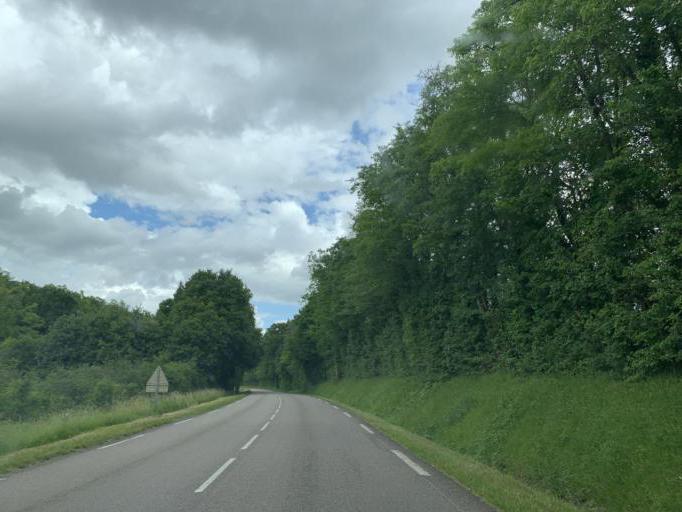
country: FR
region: Bourgogne
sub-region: Departement de l'Yonne
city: Chablis
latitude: 47.7331
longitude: 3.8023
